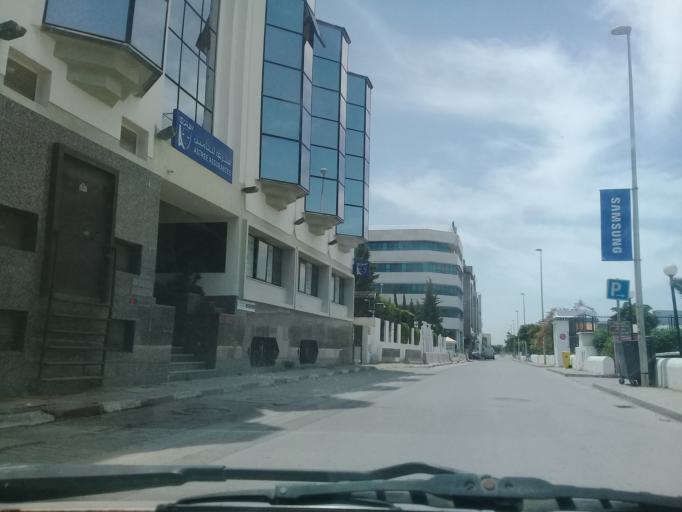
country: TN
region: Ariana
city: Ariana
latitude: 36.8369
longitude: 10.2316
